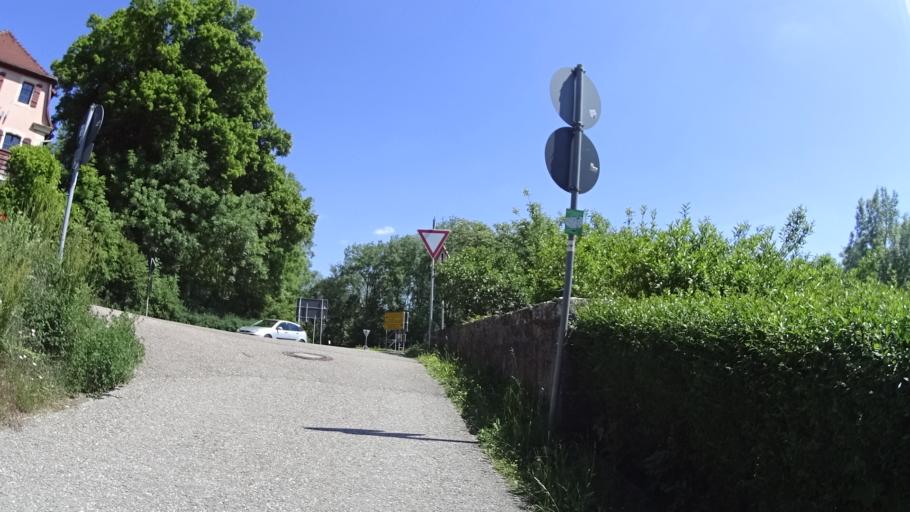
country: DE
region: Bavaria
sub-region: Regierungsbezirk Mittelfranken
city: Gebsattel
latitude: 49.3623
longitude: 10.1918
